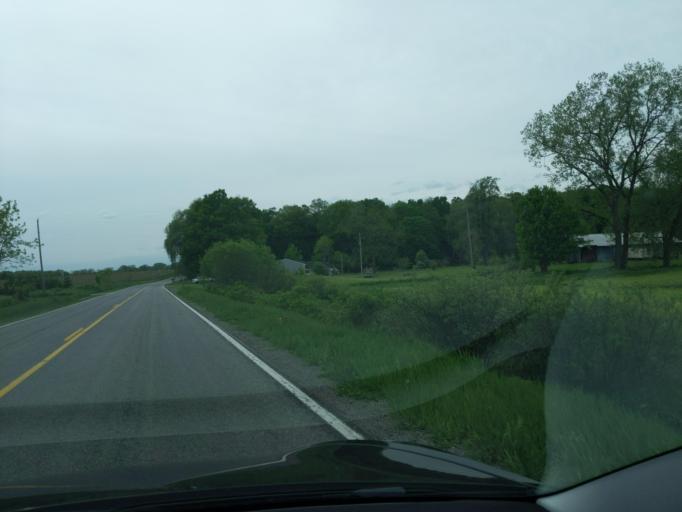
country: US
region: Michigan
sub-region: Ingham County
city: Leslie
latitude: 42.4479
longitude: -84.3617
